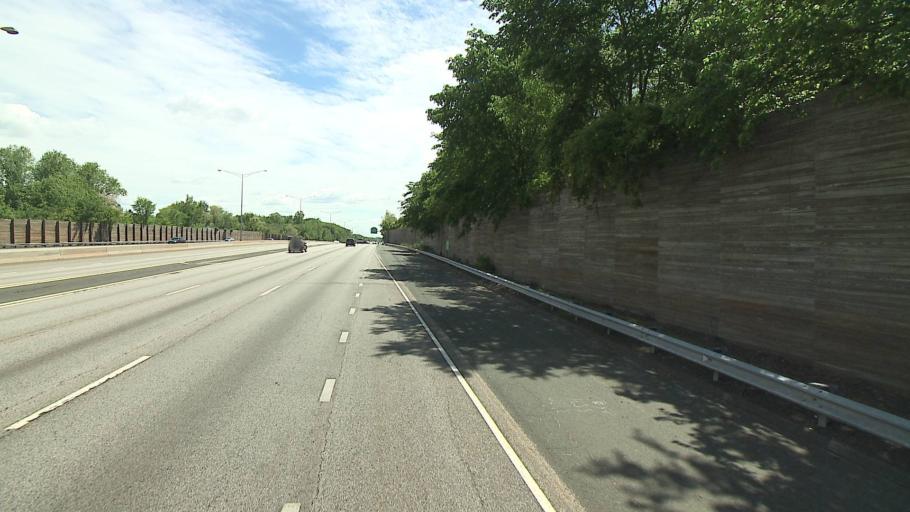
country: US
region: Connecticut
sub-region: Hartford County
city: Windsor
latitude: 41.8481
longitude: -72.6652
